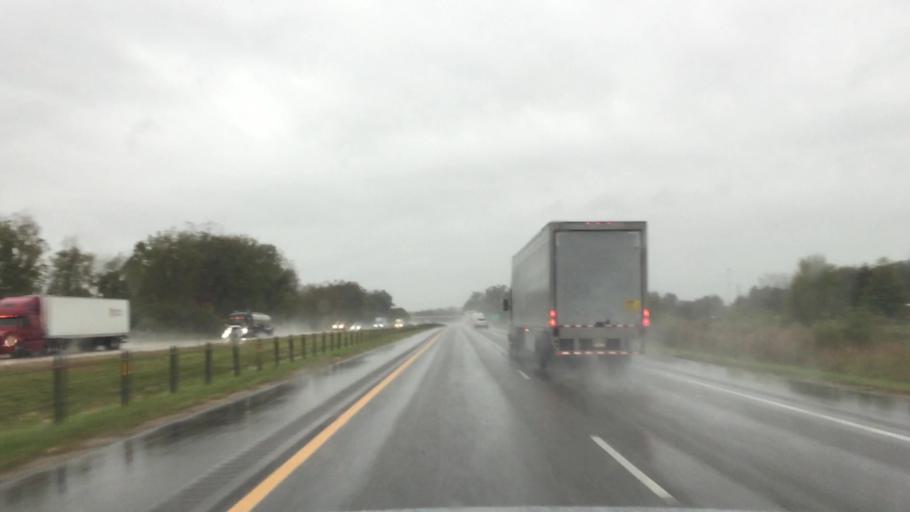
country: US
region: Michigan
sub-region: Van Buren County
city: Hartford
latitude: 42.1938
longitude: -86.1367
